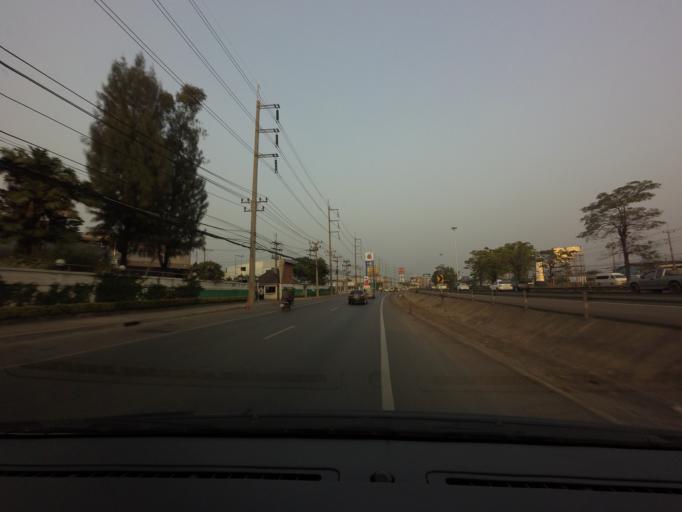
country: TH
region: Samut Sakhon
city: Samut Sakhon
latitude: 13.5929
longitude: 100.3368
